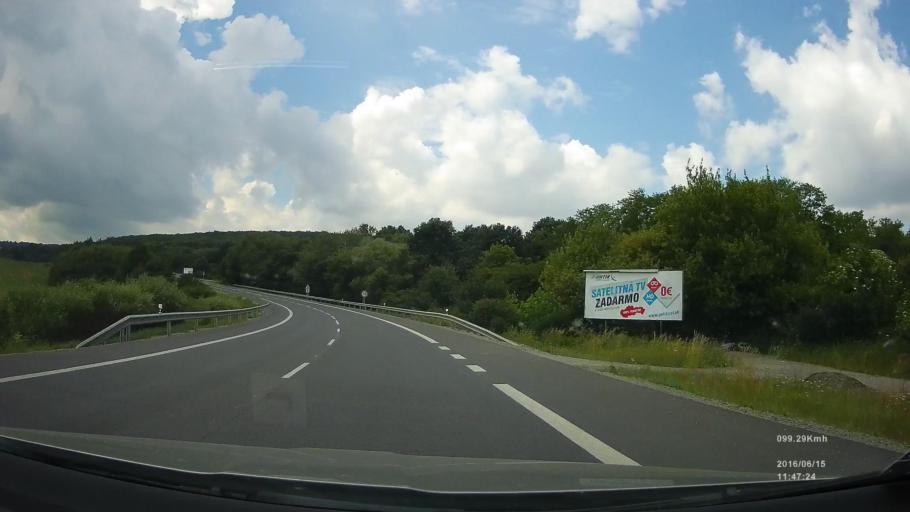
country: SK
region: Kosicky
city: Kosice
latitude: 48.7321
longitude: 21.3302
